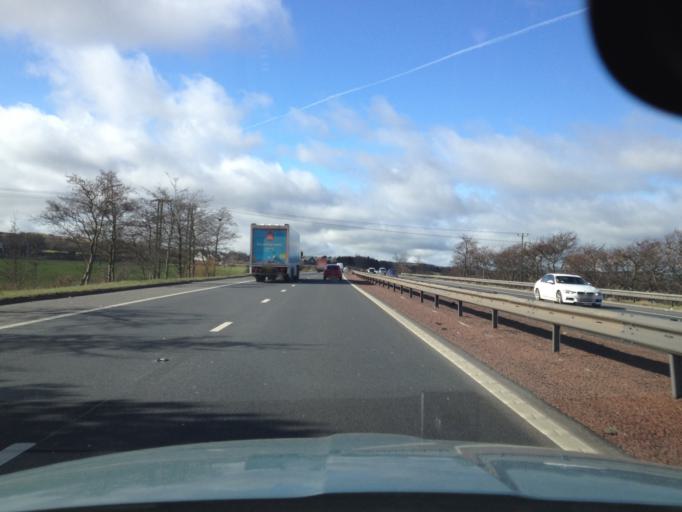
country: GB
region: Scotland
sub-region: West Lothian
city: Broxburn
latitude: 55.9216
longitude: -3.4686
